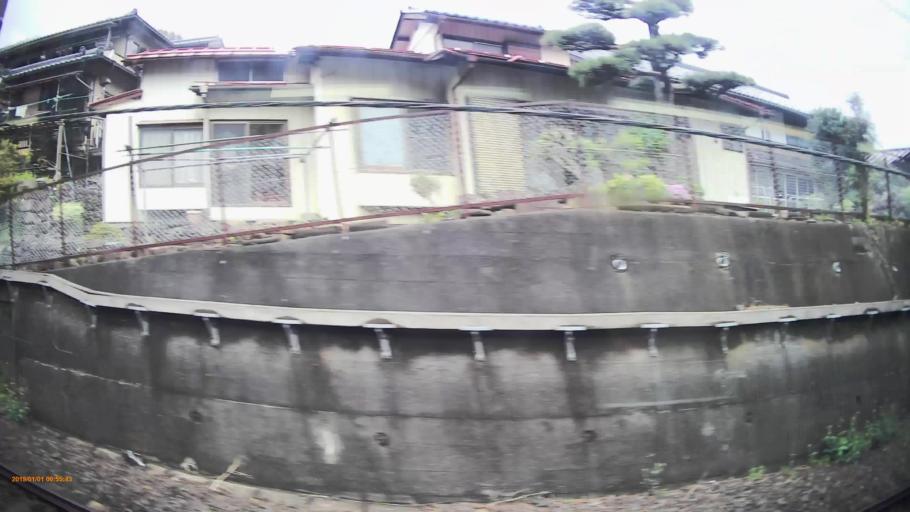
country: JP
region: Yamanashi
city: Otsuki
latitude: 35.6024
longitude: 138.8435
